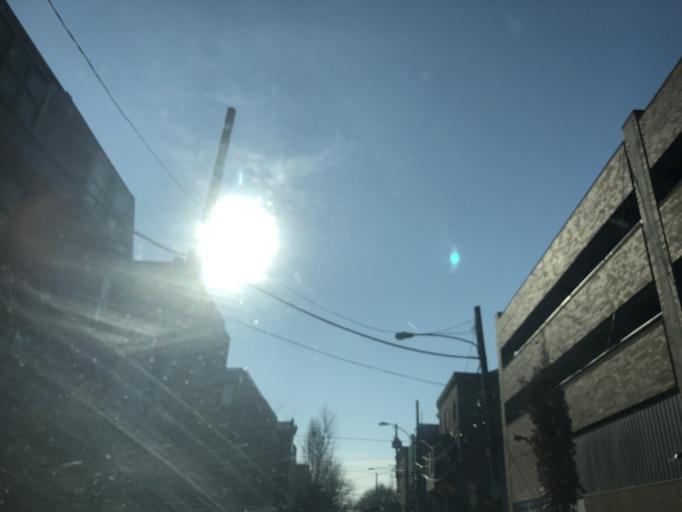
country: US
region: Pennsylvania
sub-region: Philadelphia County
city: Philadelphia
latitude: 39.9442
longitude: -75.1703
